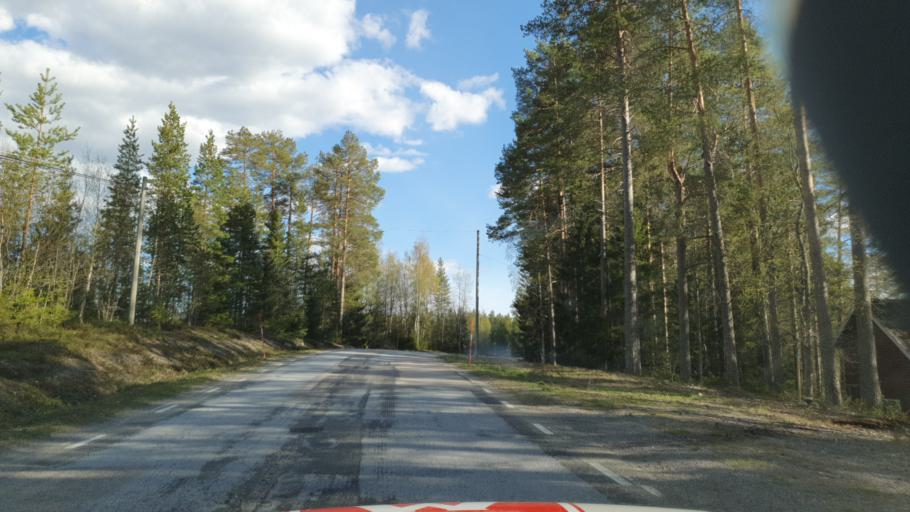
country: SE
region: Vaesterbotten
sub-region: Umea Kommun
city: Roback
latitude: 63.9055
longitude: 20.1525
